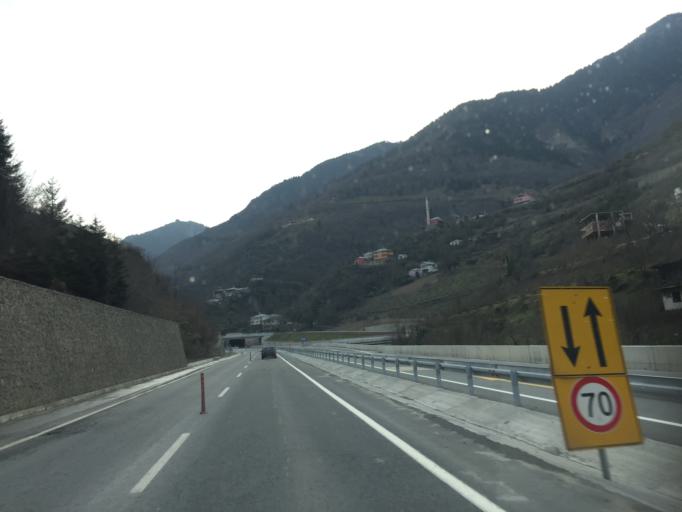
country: TR
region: Trabzon
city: Macka
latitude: 40.7818
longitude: 39.5723
